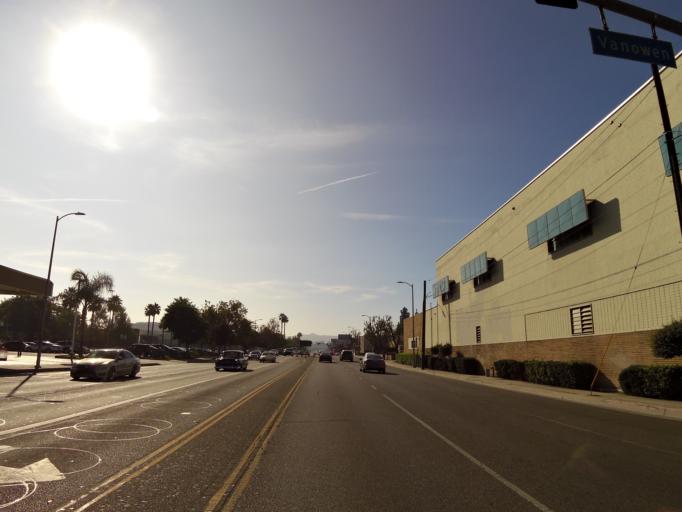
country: US
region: California
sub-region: Los Angeles County
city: Canoga Park
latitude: 34.1937
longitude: -118.6060
